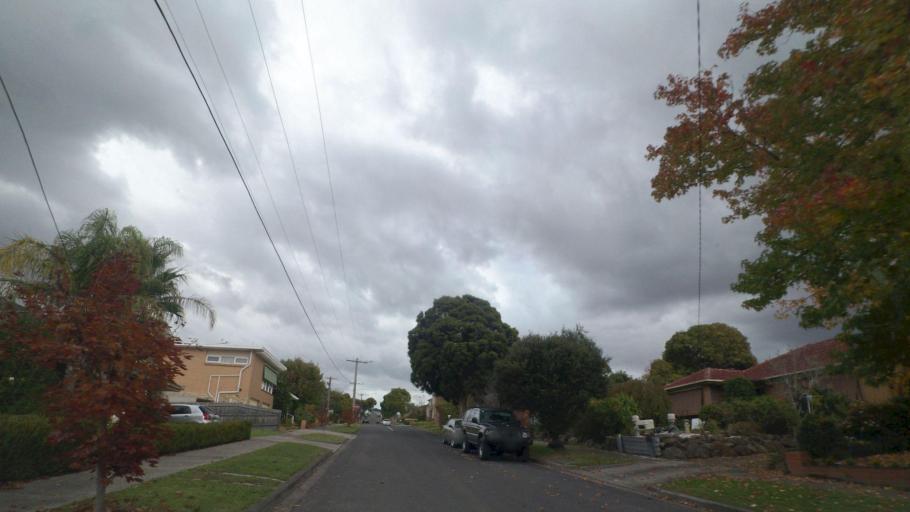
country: AU
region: Victoria
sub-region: Manningham
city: Doncaster East
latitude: -37.7849
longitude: 145.1570
